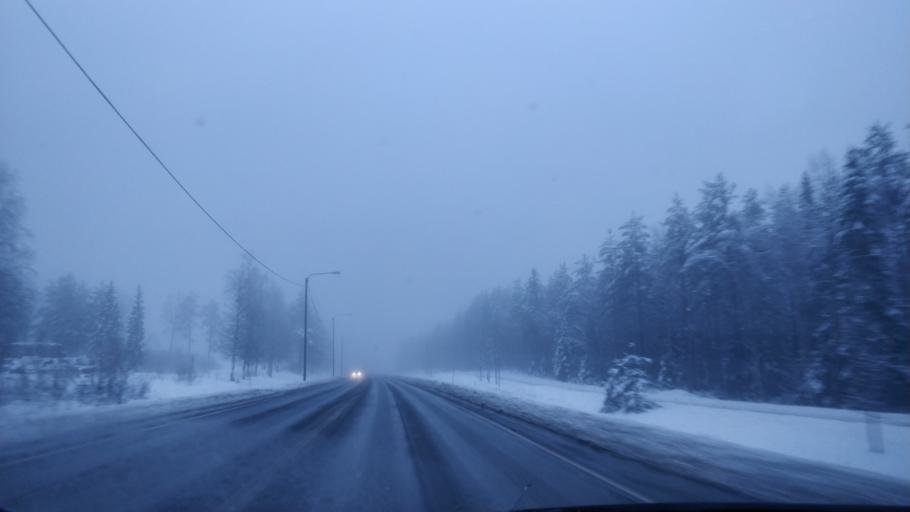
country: FI
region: Lapland
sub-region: Kemi-Tornio
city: Tervola
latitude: 66.1349
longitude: 24.9215
